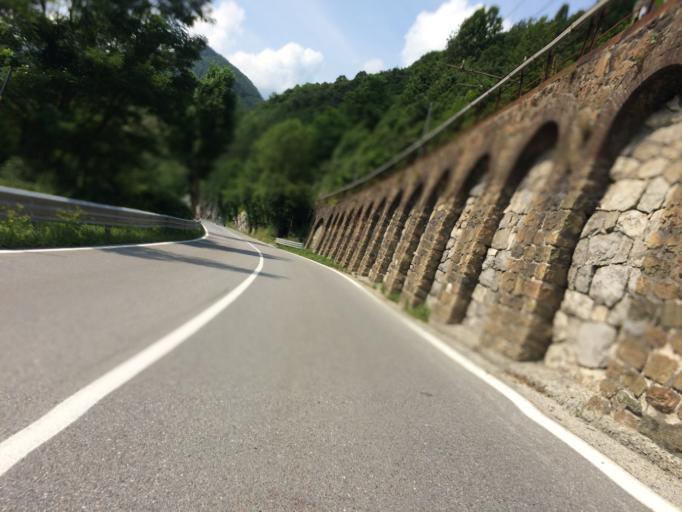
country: IT
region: Piedmont
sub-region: Provincia di Cuneo
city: Vernante
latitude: 44.2594
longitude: 7.5237
